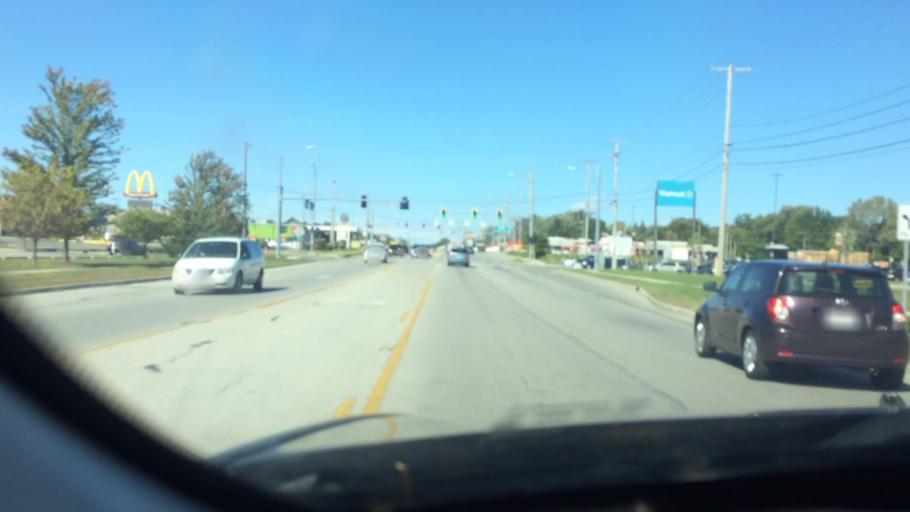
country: US
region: Ohio
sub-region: Lucas County
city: Ottawa Hills
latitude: 41.6740
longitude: -83.6826
